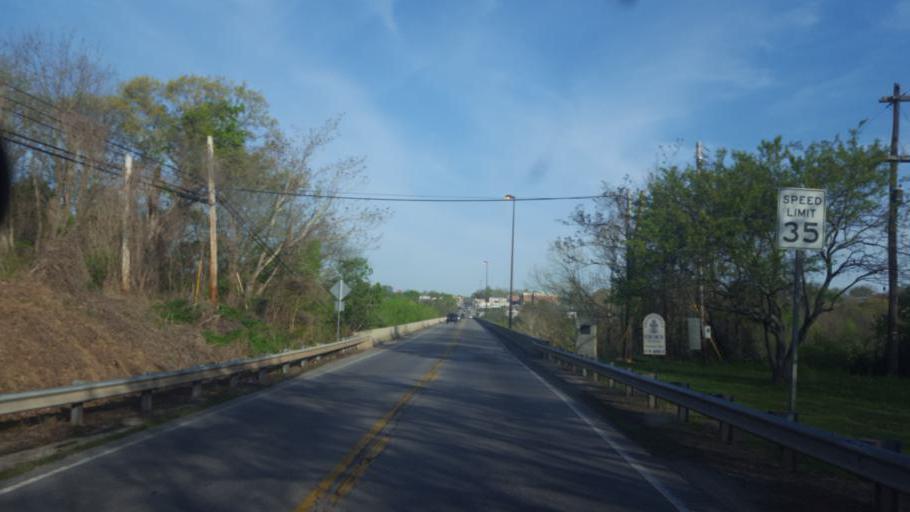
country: US
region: Kentucky
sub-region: Hart County
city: Munfordville
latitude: 37.2671
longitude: -85.8827
